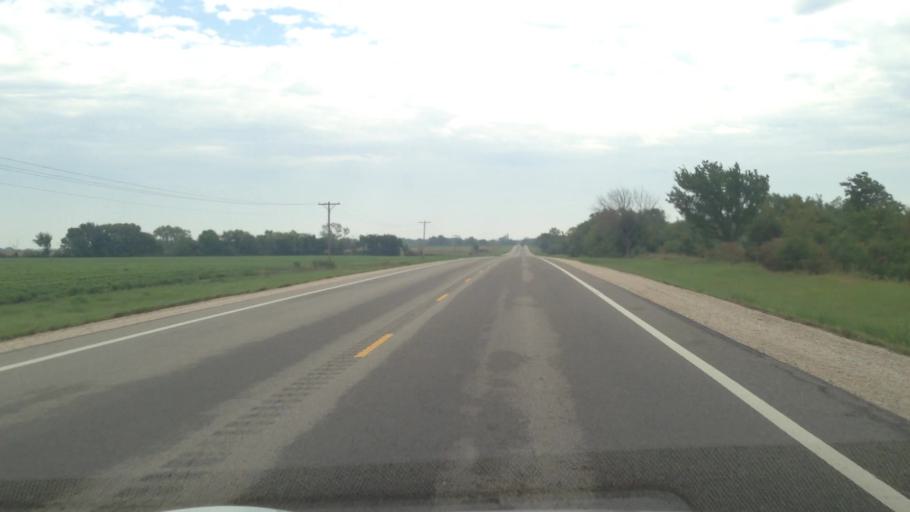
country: US
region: Kansas
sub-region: Allen County
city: Iola
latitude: 37.9050
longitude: -95.0940
